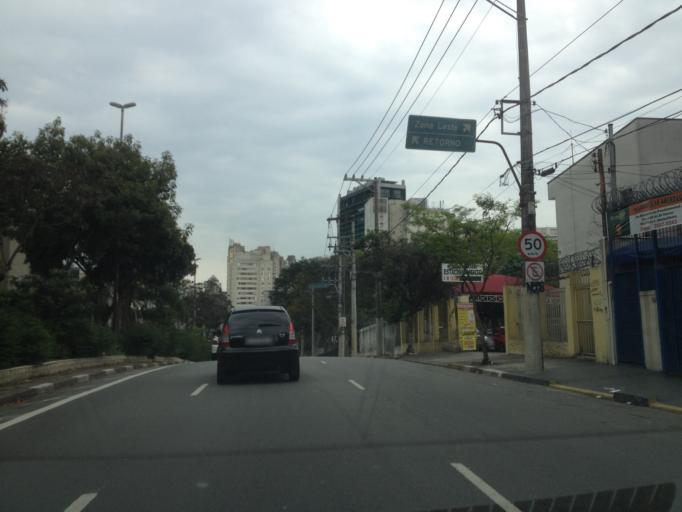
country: BR
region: Sao Paulo
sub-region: Sao Paulo
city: Sao Paulo
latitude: -23.5547
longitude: -46.6457
